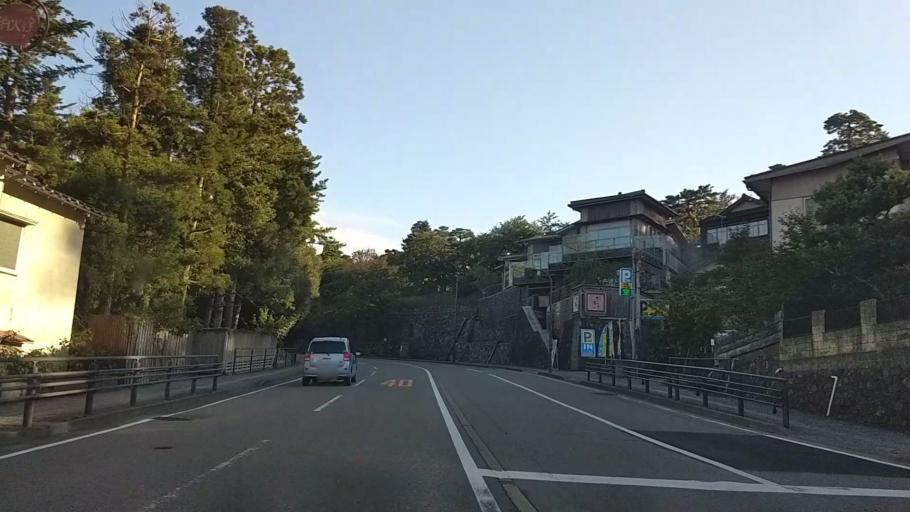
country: JP
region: Ishikawa
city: Kanazawa-shi
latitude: 36.5644
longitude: 136.6635
